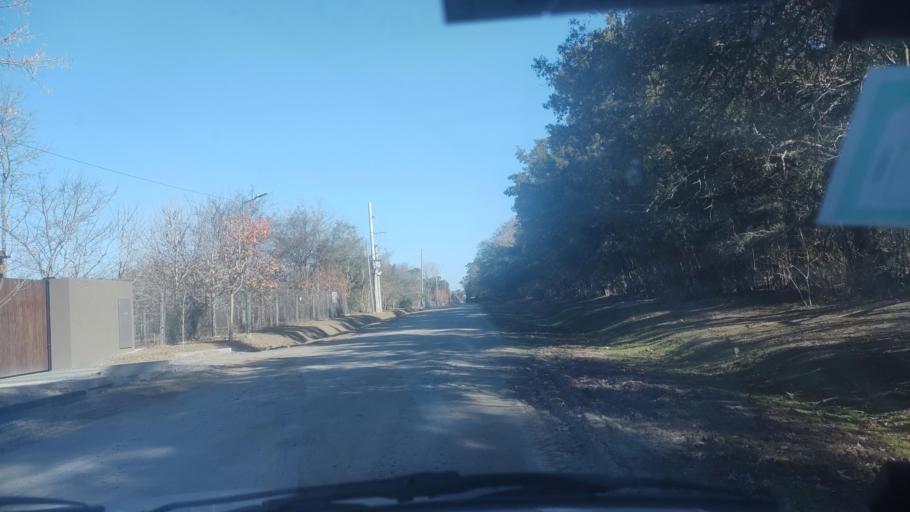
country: AR
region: Buenos Aires
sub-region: Partido de La Plata
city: La Plata
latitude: -34.8548
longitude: -58.1079
